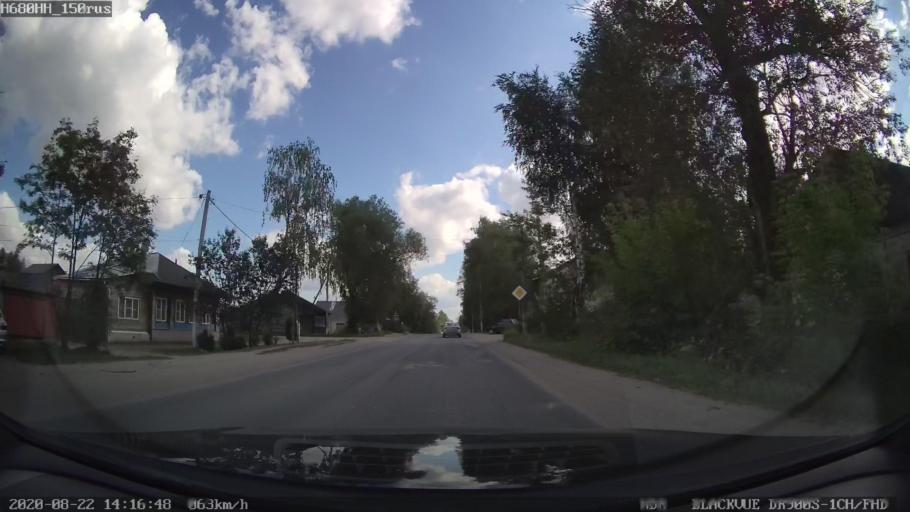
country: RU
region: Tverskaya
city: Bezhetsk
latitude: 57.7736
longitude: 36.7003
